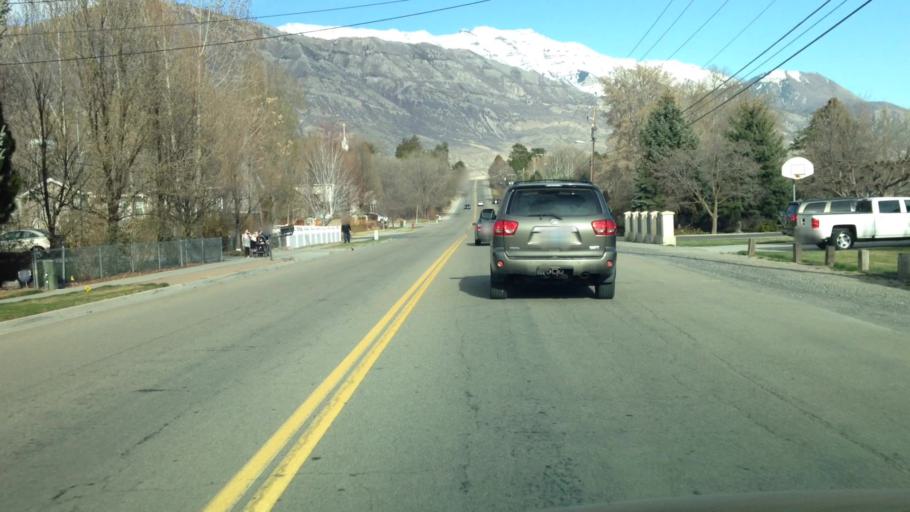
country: US
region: Utah
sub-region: Utah County
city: American Fork
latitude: 40.3918
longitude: -111.7804
